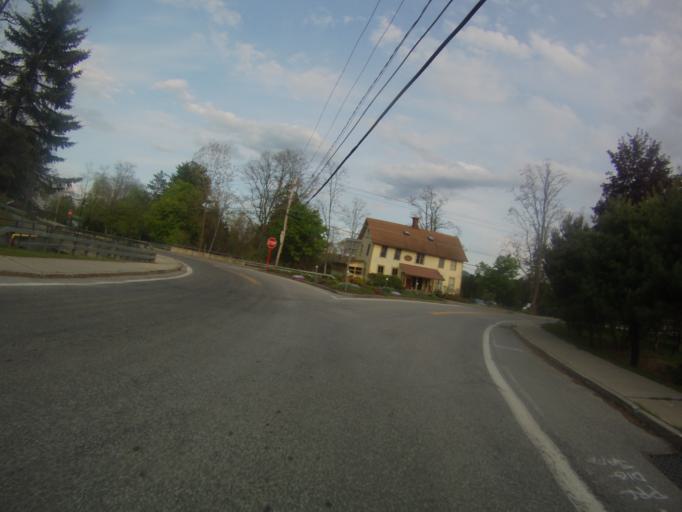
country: US
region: New York
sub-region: Essex County
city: Ticonderoga
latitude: 43.7455
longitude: -73.4989
